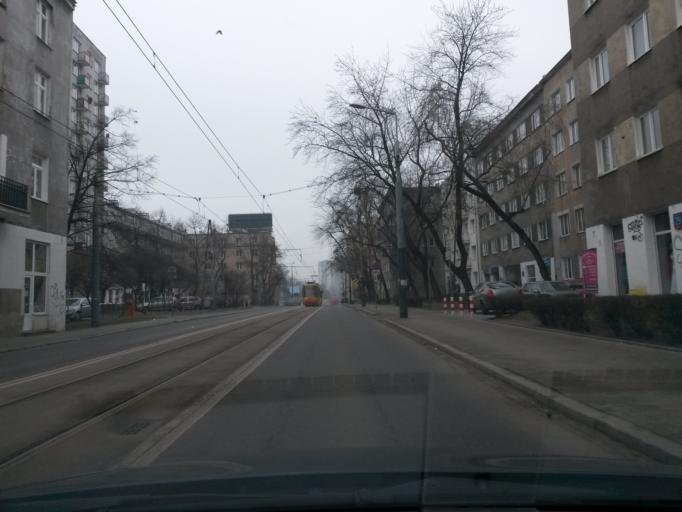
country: PL
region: Masovian Voivodeship
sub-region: Warszawa
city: Wola
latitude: 52.2388
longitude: 20.9713
